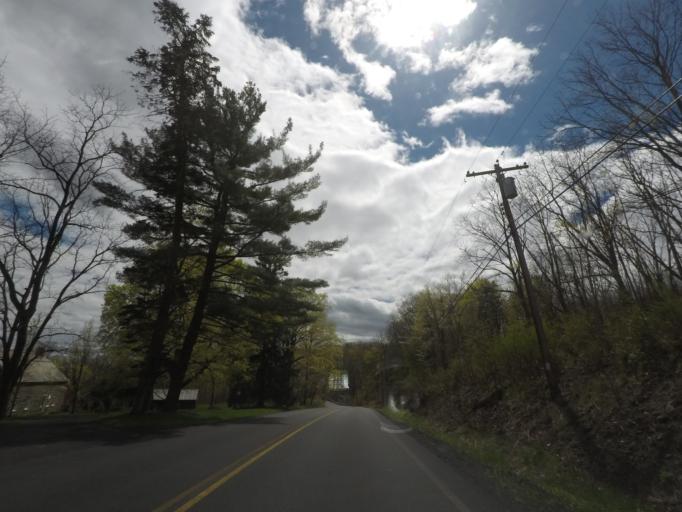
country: US
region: New York
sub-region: Albany County
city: Ravena
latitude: 42.4670
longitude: -73.7918
